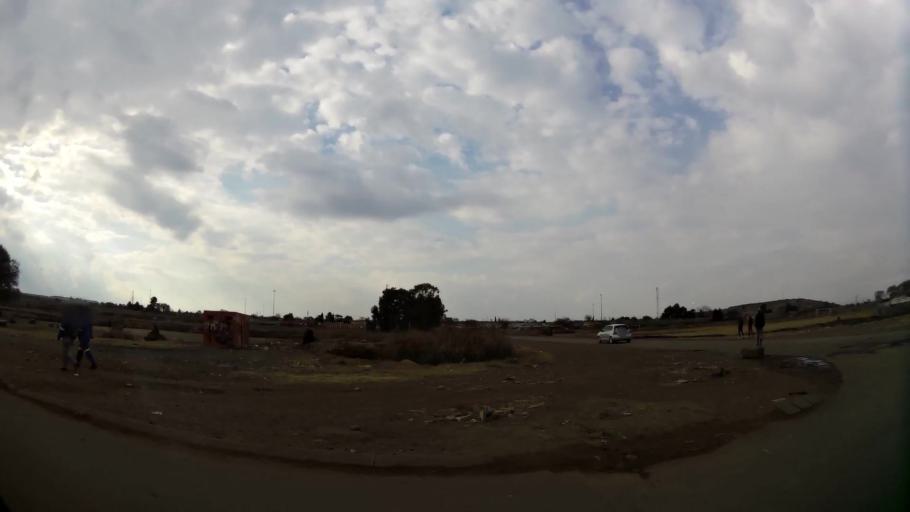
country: ZA
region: Gauteng
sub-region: Sedibeng District Municipality
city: Vanderbijlpark
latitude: -26.6713
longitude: 27.8476
